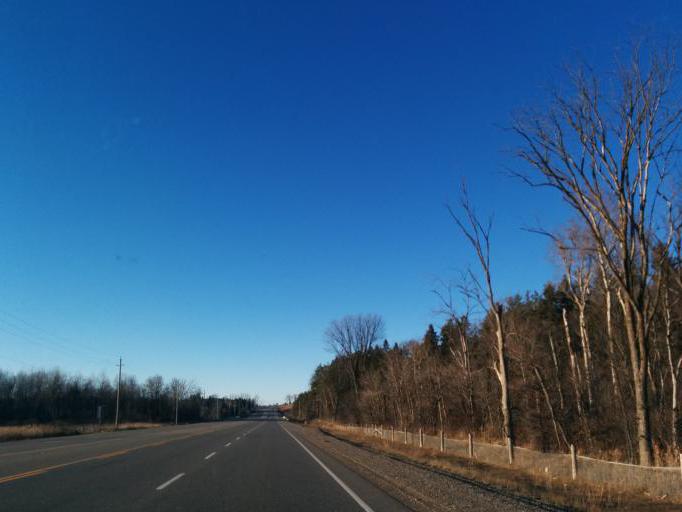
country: CA
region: Ontario
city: Orangeville
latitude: 43.9073
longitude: -80.0600
